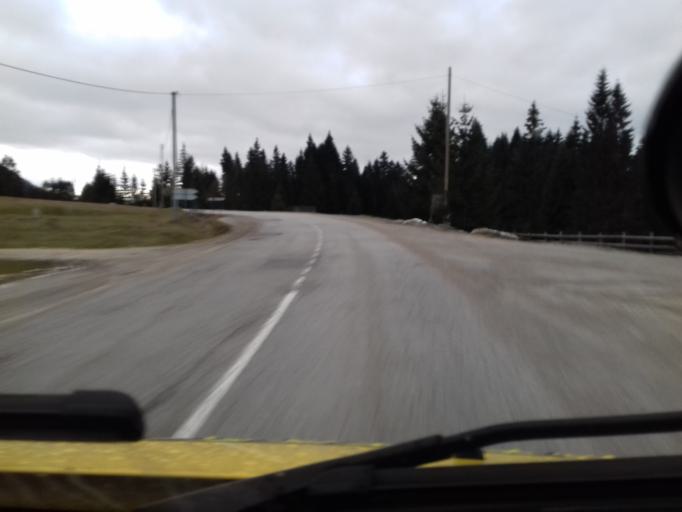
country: BA
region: Federation of Bosnia and Herzegovina
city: Turbe
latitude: 44.3026
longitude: 17.4933
